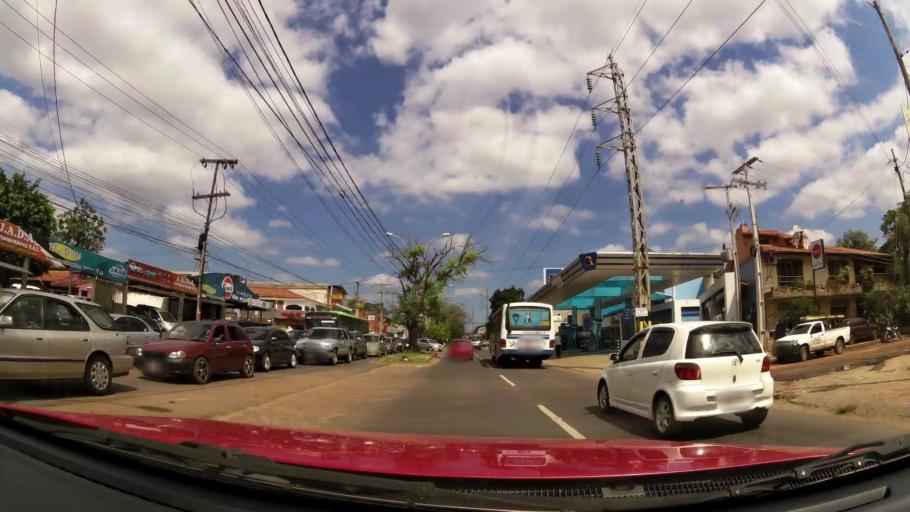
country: PY
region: Central
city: Fernando de la Mora
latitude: -25.3072
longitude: -57.5336
